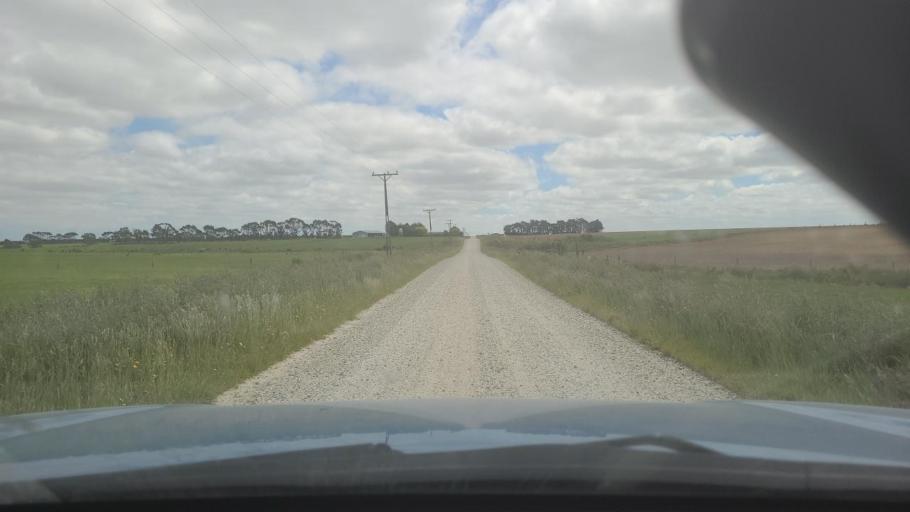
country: NZ
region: Southland
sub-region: Invercargill City
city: Invercargill
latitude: -46.3306
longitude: 168.5990
